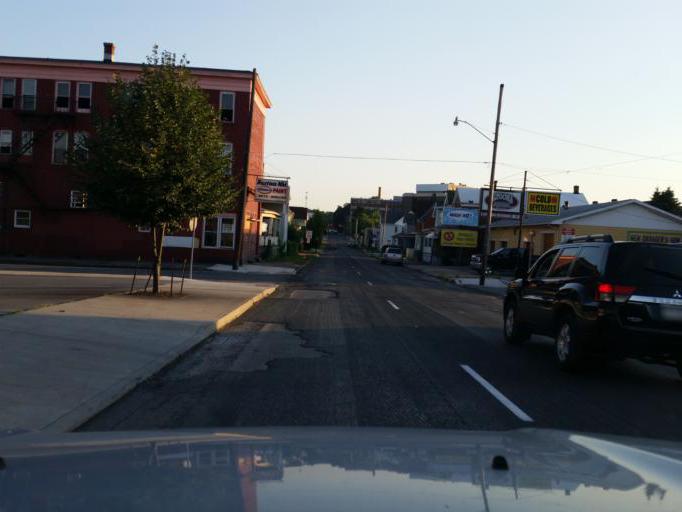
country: US
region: Pennsylvania
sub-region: Blair County
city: Altoona
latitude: 40.5039
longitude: -78.4051
